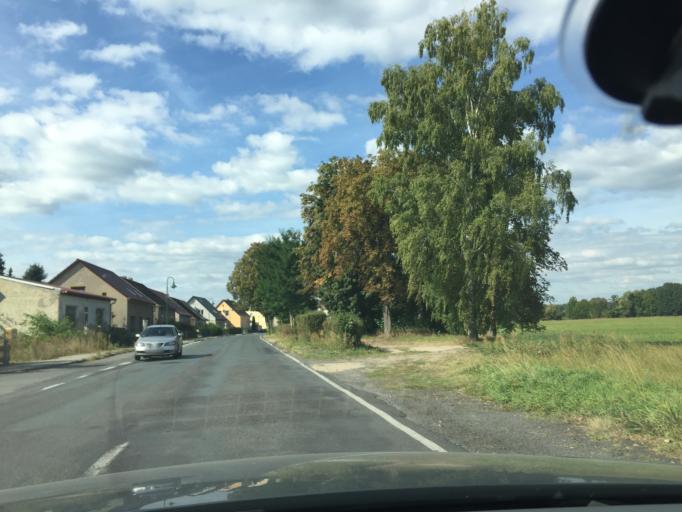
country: DE
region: Brandenburg
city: Spreenhagen
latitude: 52.3569
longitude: 13.8478
